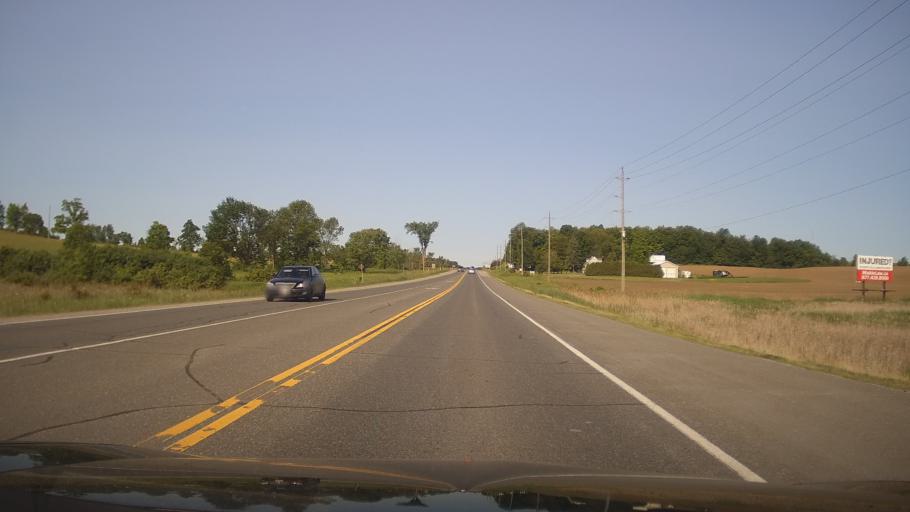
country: CA
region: Ontario
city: Peterborough
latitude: 44.3216
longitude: -78.1662
